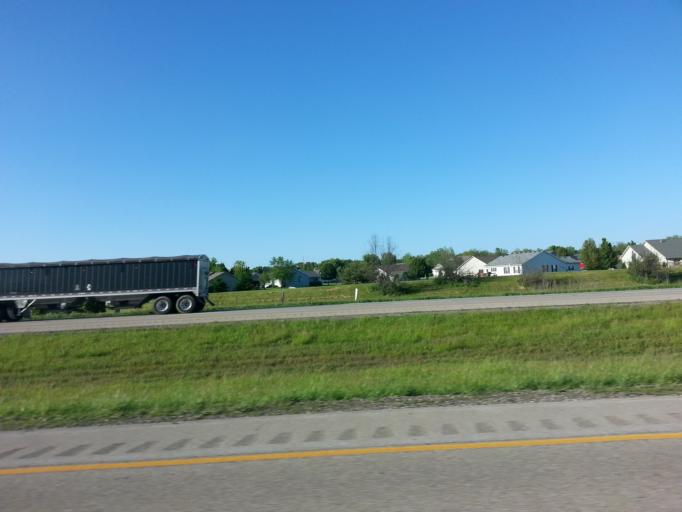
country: US
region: Illinois
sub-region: McLean County
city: Downs
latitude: 40.3921
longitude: -88.8817
